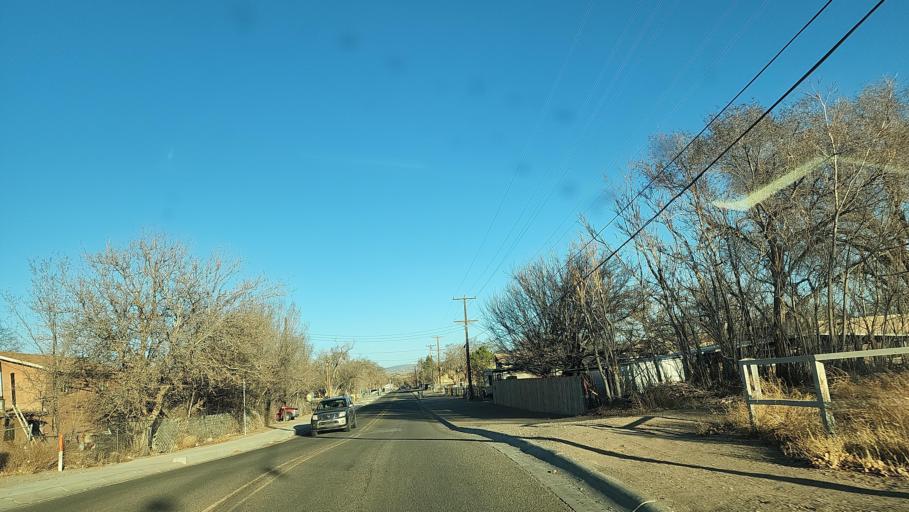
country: US
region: New Mexico
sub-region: Bernalillo County
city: South Valley
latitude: 35.0306
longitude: -106.6854
